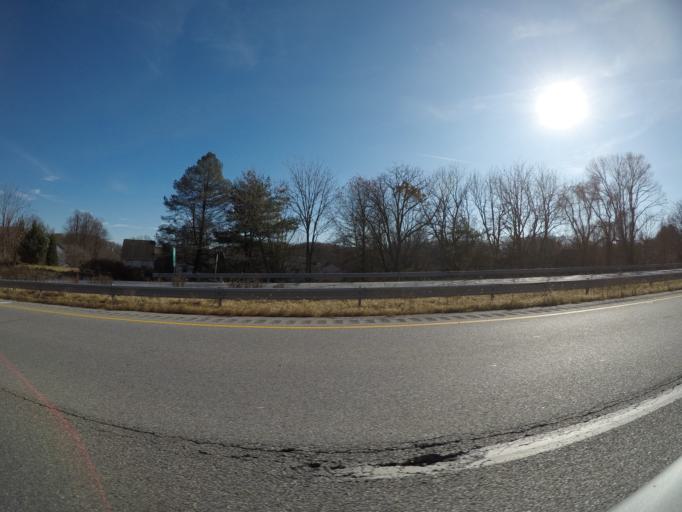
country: US
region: Pennsylvania
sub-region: Chester County
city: Coatesville
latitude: 39.9939
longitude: -75.8529
